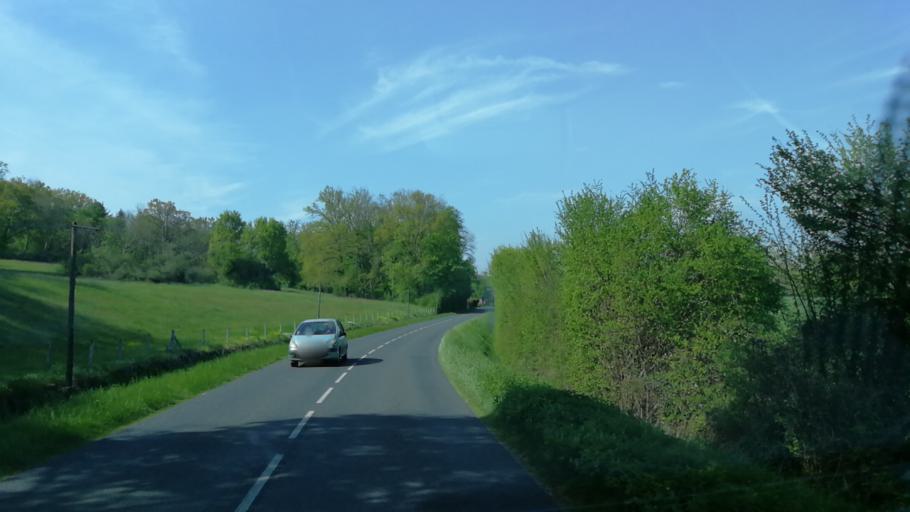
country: FR
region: Auvergne
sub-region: Departement de l'Allier
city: Saint-Gerand-le-Puy
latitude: 46.3458
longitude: 3.5787
